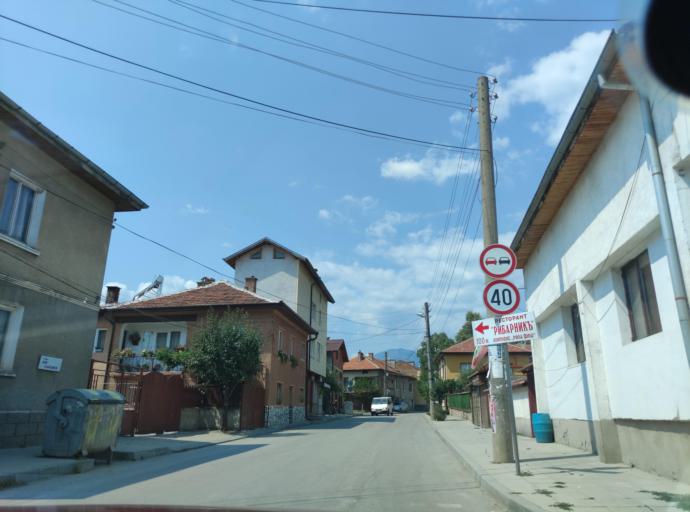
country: BG
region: Blagoevgrad
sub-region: Obshtina Belitsa
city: Belitsa
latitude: 41.9478
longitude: 23.5576
